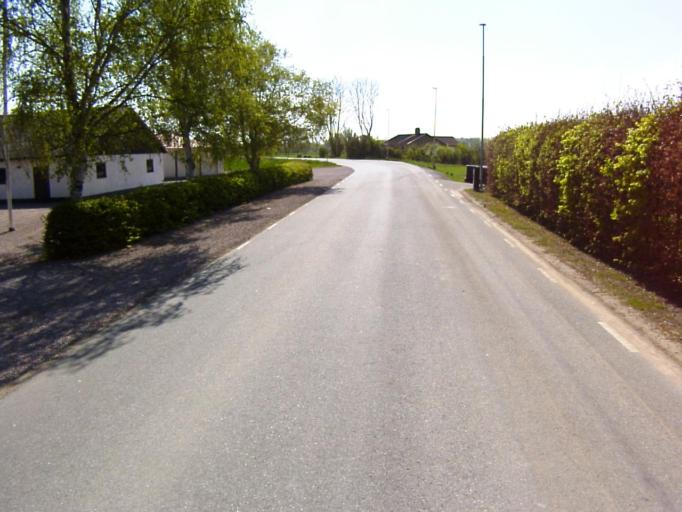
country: SE
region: Skane
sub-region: Kristianstads Kommun
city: Kristianstad
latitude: 56.0217
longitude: 14.2148
